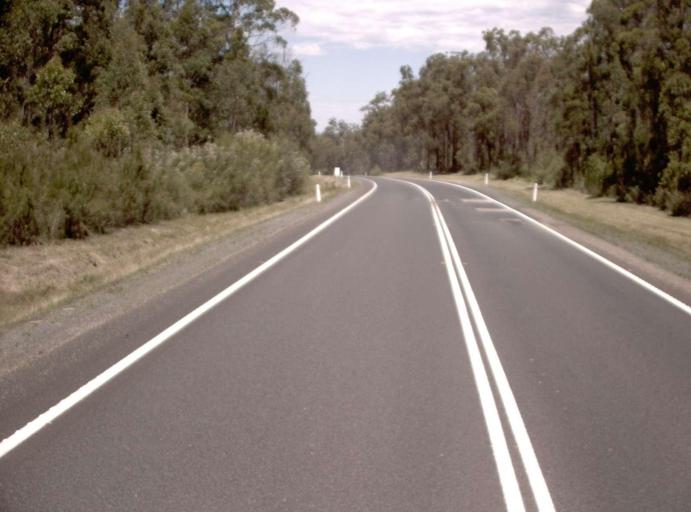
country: AU
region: New South Wales
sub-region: Bombala
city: Bombala
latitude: -37.5662
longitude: 149.1241
